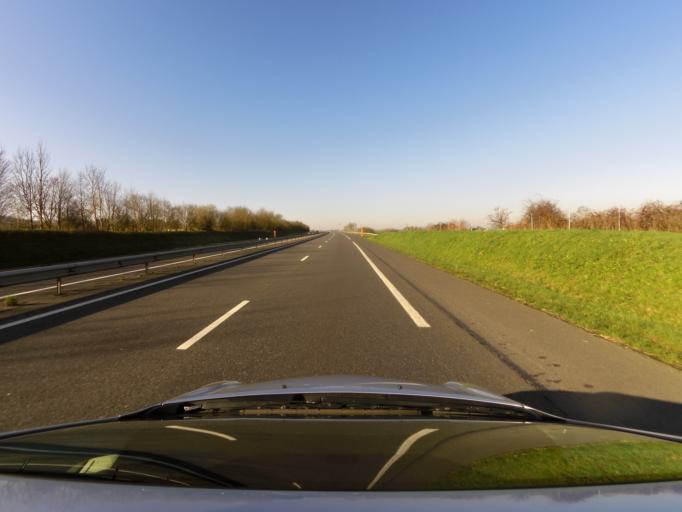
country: FR
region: Lower Normandy
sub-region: Departement du Calvados
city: Saint-Martin-des-Besaces
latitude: 49.0304
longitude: -0.8259
